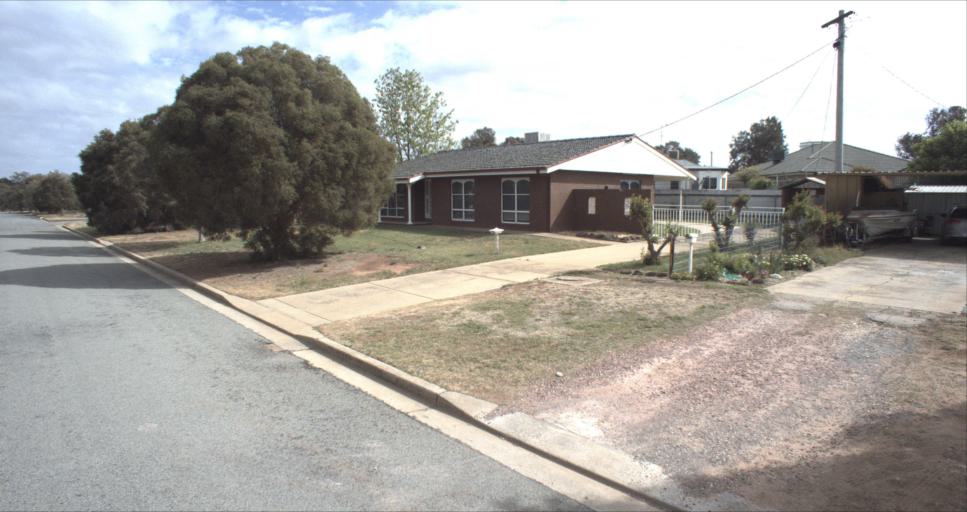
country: AU
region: New South Wales
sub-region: Leeton
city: Leeton
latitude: -34.5645
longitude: 146.3951
